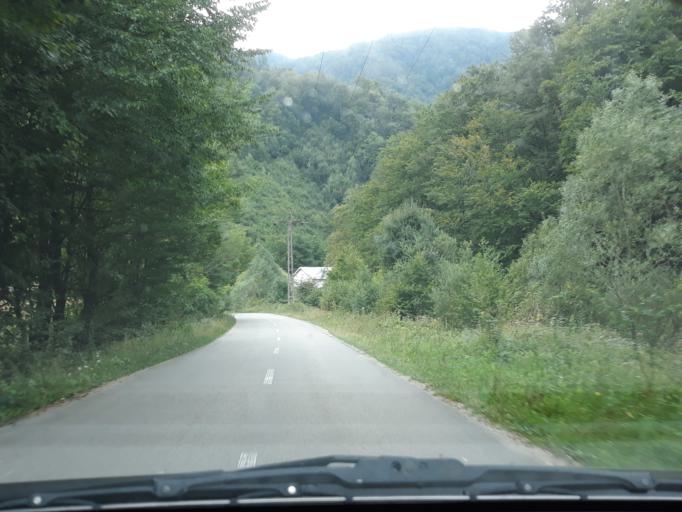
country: RO
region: Bihor
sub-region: Comuna Pietroasa
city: Pietroasa
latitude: 46.5910
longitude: 22.6321
